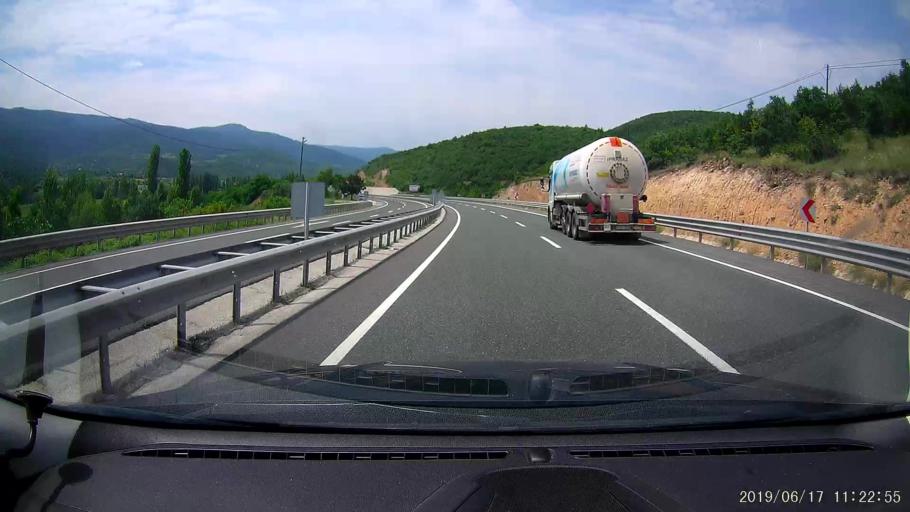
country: TR
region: Cankiri
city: Ilgaz
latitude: 40.8957
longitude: 33.7426
